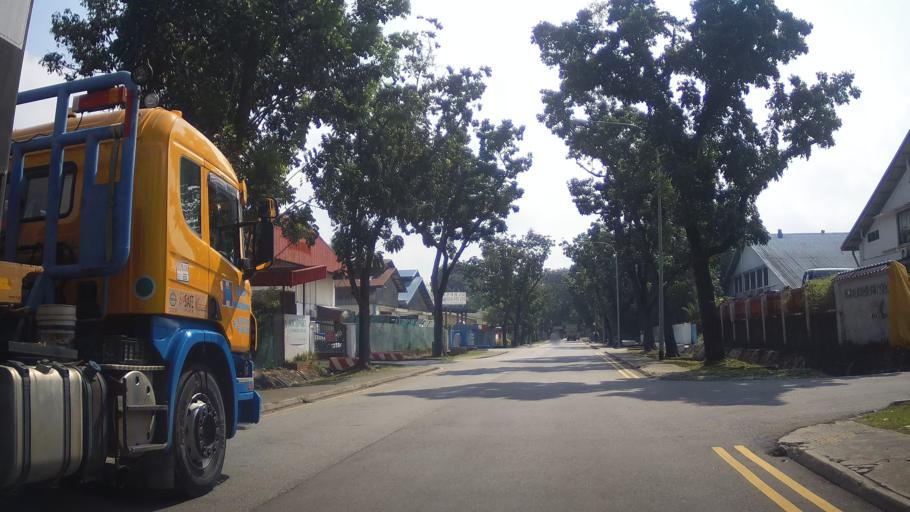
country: MY
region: Johor
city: Johor Bahru
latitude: 1.3264
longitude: 103.7007
